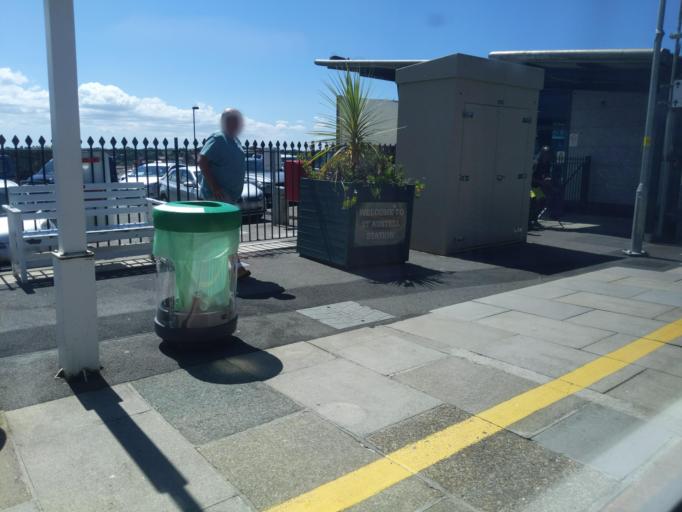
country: GB
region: England
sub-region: Cornwall
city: St Austell
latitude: 50.3395
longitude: -4.7890
